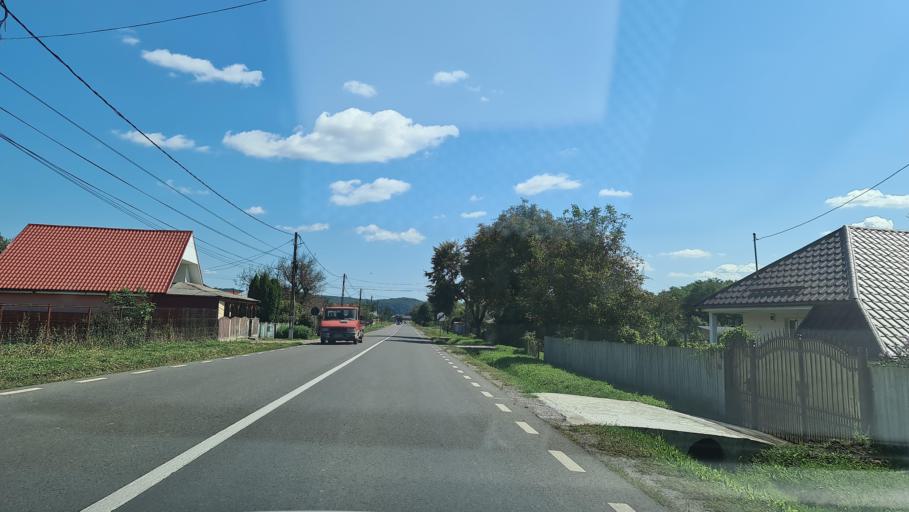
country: RO
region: Bacau
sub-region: Comuna Scorteni
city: Scorteni
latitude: 46.5307
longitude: 26.6373
